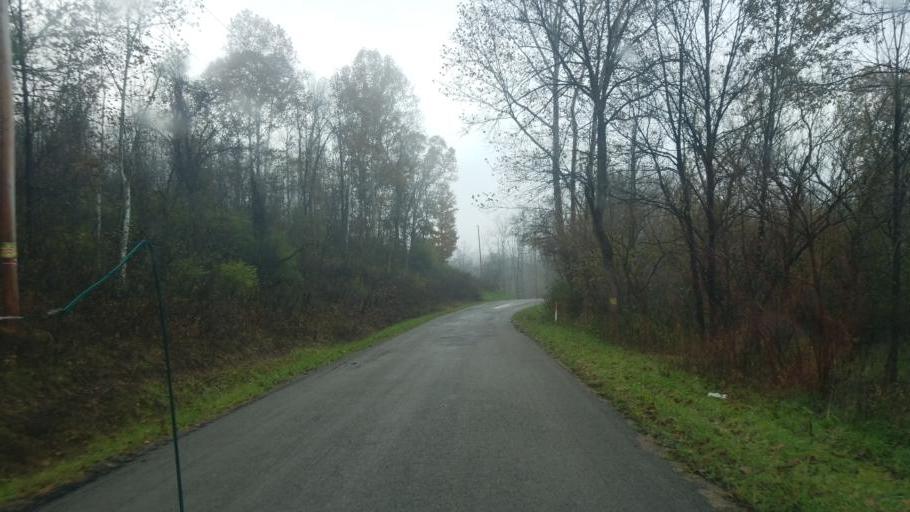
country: US
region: Ohio
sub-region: Athens County
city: Glouster
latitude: 39.4524
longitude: -81.9262
